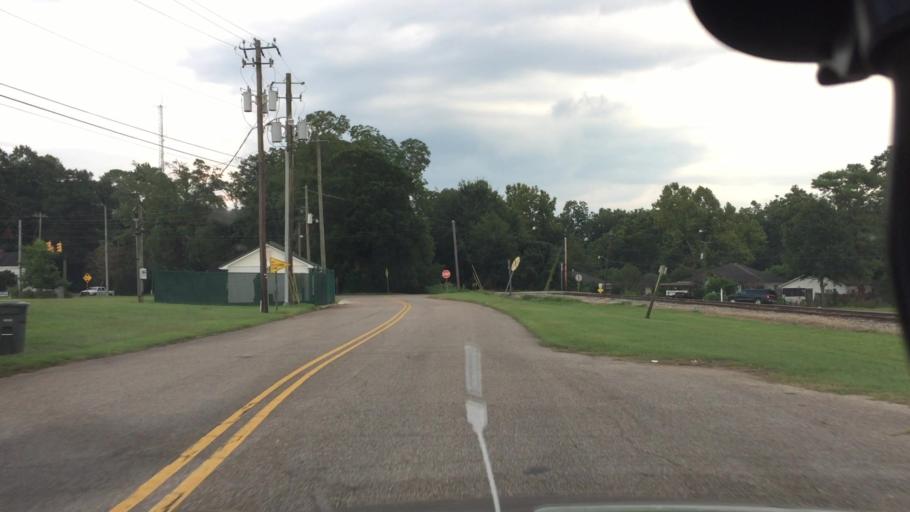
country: US
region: Alabama
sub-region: Coffee County
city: Enterprise
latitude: 31.3118
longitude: -85.8528
